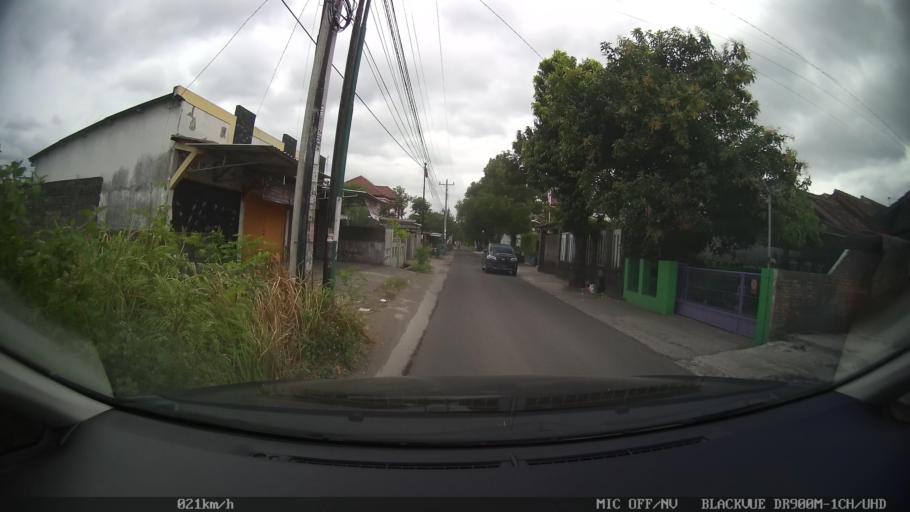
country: ID
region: Daerah Istimewa Yogyakarta
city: Depok
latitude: -7.8174
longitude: 110.4163
